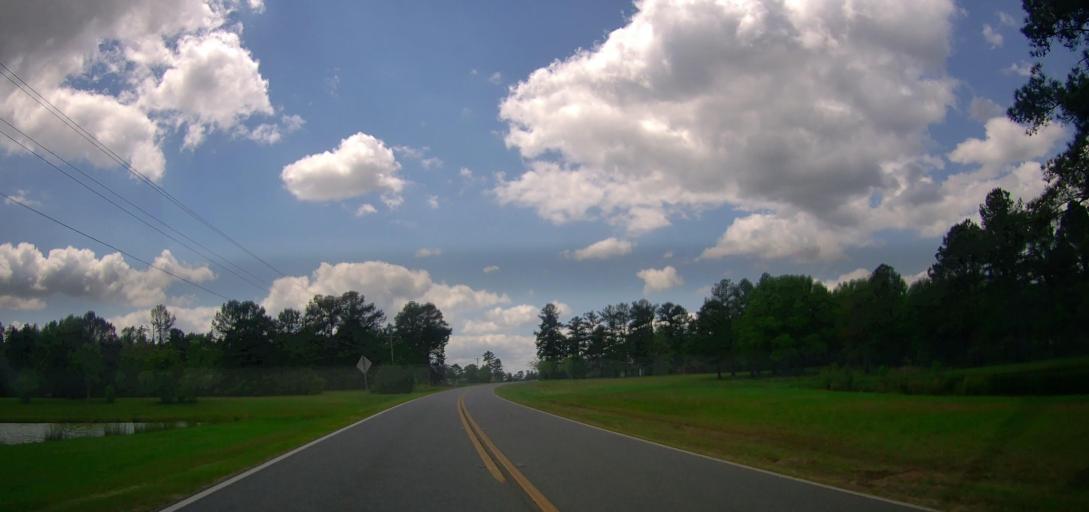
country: US
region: Georgia
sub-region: Laurens County
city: East Dublin
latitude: 32.5186
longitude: -82.7807
